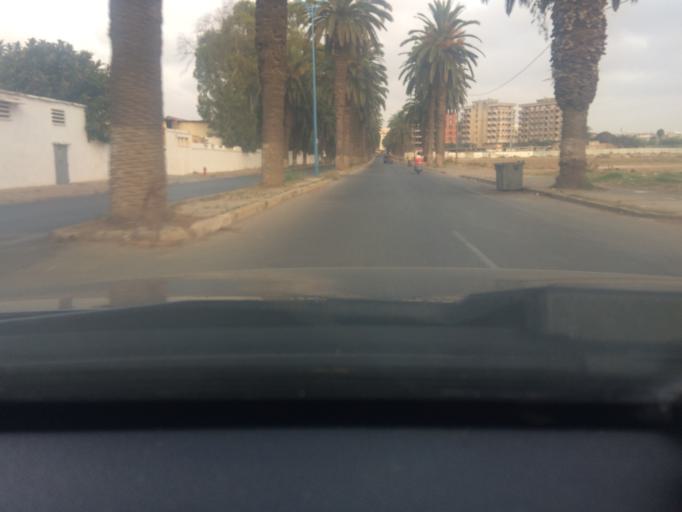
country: MA
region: Grand Casablanca
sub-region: Mohammedia
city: Mohammedia
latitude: 33.6952
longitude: -7.3971
